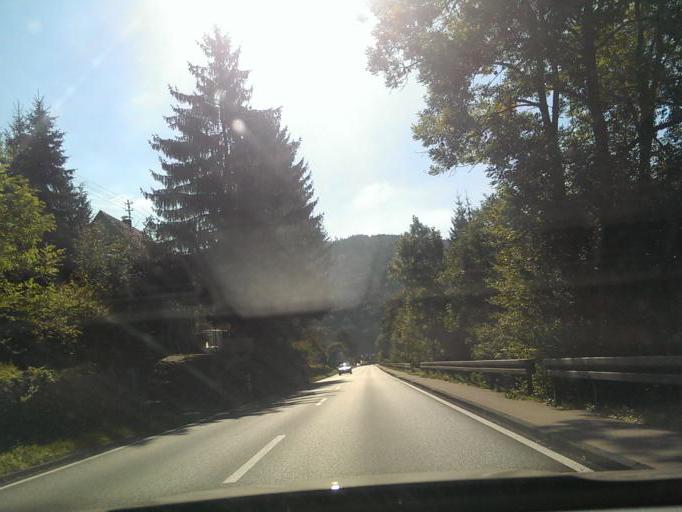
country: DE
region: Baden-Wuerttemberg
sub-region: Karlsruhe Region
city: Hofen an der Enz
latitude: 48.7825
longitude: 8.5790
